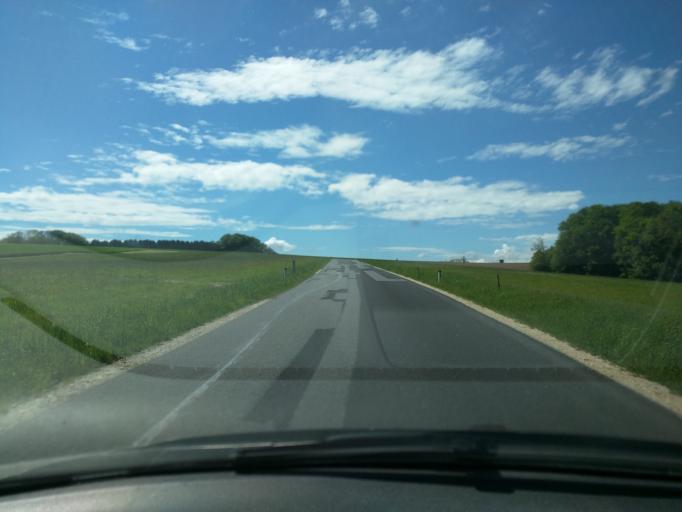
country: AT
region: Lower Austria
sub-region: Politischer Bezirk Amstetten
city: Sankt Georgen am Ybbsfelde
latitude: 48.1409
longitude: 14.9105
